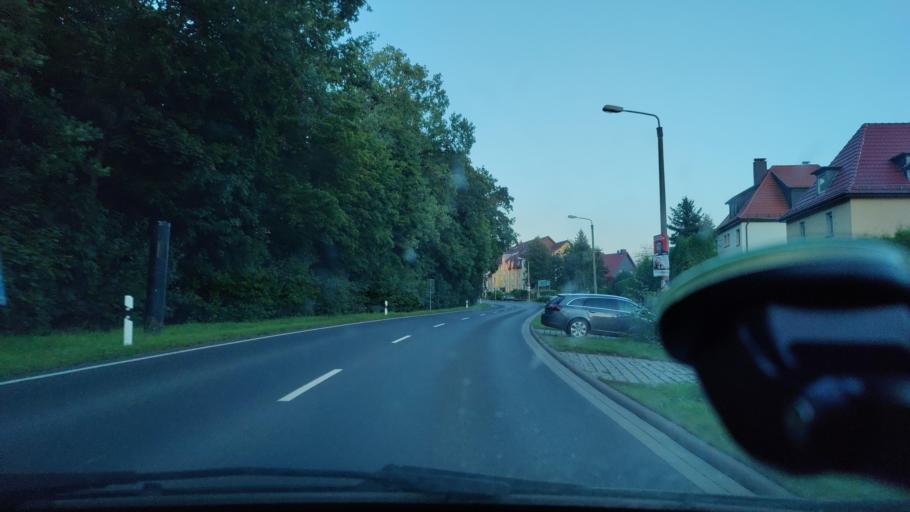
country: DE
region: Thuringia
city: Weimar
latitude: 50.9797
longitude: 11.3501
